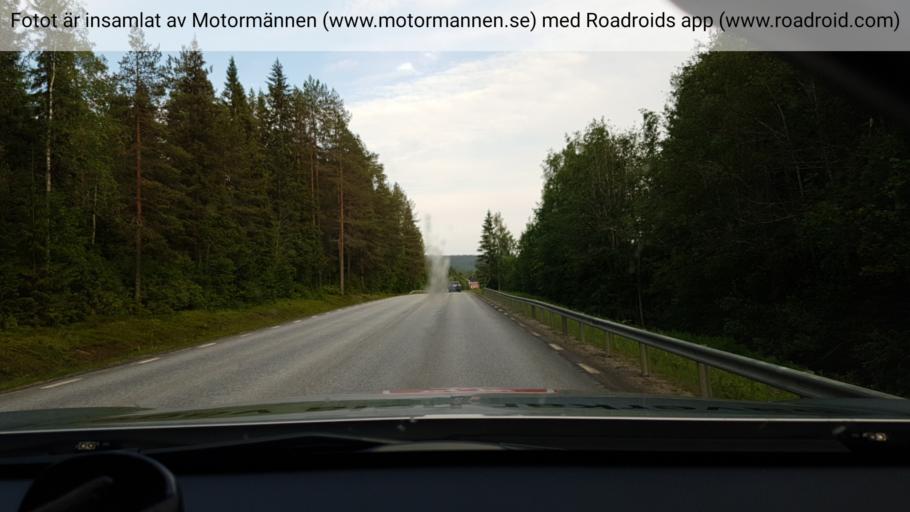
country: SE
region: Vaesterbotten
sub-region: Vannas Kommun
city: Vaennaes
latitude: 63.9667
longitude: 19.7461
